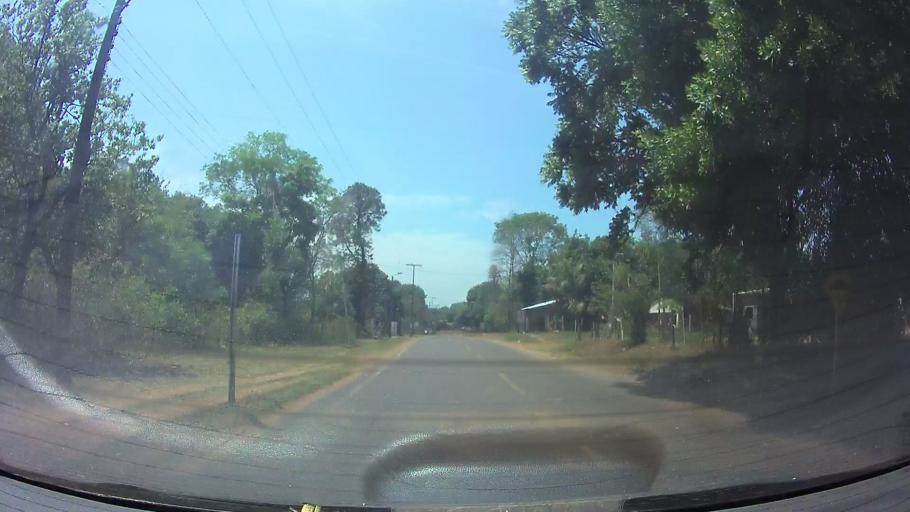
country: PY
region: Central
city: Ita
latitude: -25.4371
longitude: -57.3987
